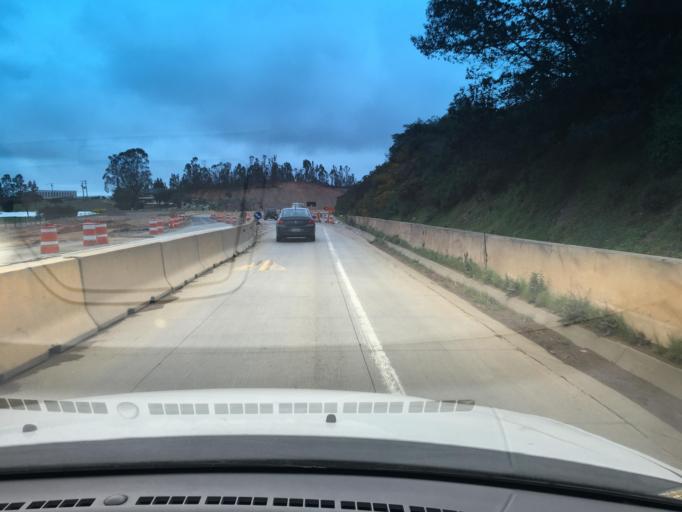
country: CL
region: Valparaiso
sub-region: Provincia de Valparaiso
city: Valparaiso
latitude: -33.0818
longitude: -71.6215
